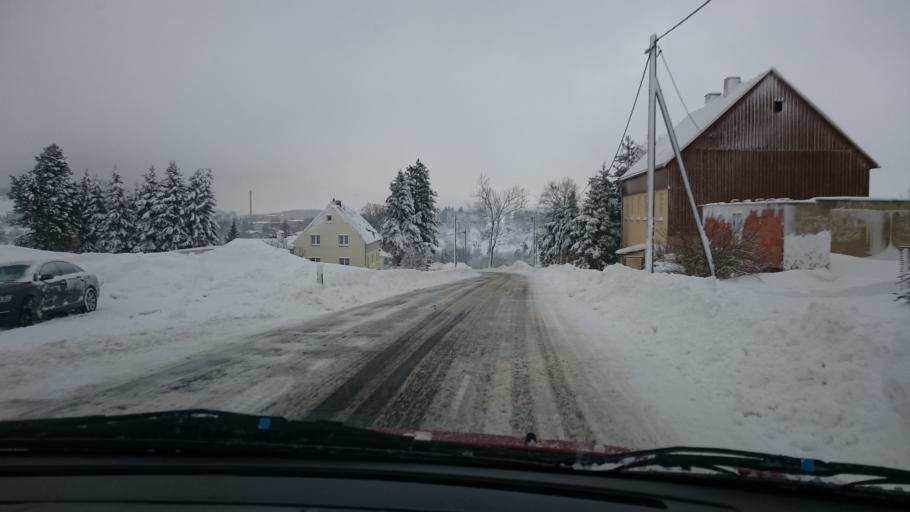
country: DE
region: Saxony
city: Geyer
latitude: 50.6183
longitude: 12.9193
